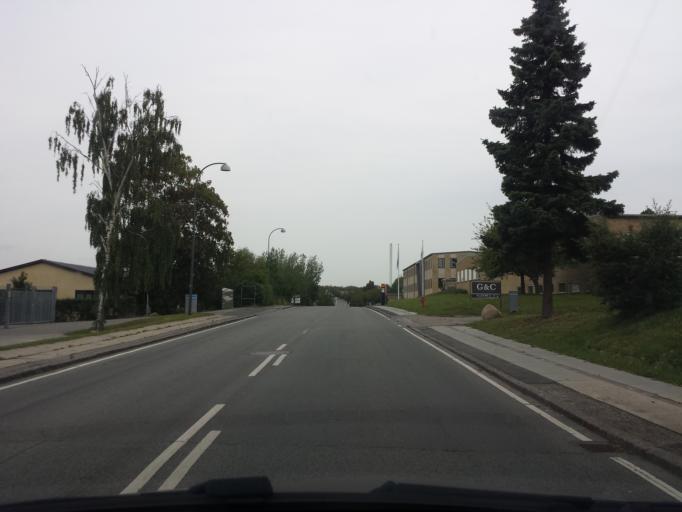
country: DK
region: Capital Region
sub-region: Herlev Kommune
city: Herlev
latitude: 55.7206
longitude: 12.4278
